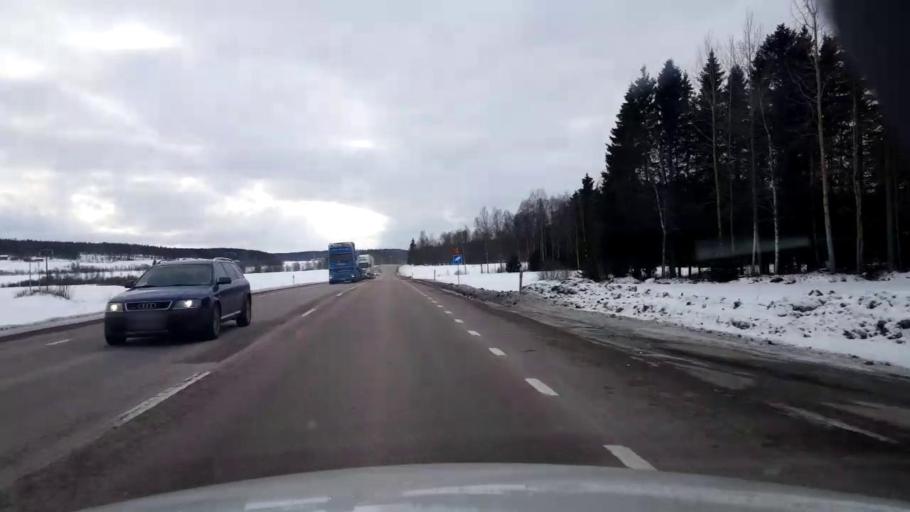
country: SE
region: Gaevleborg
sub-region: Nordanstigs Kommun
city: Bergsjoe
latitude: 62.0209
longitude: 17.2522
